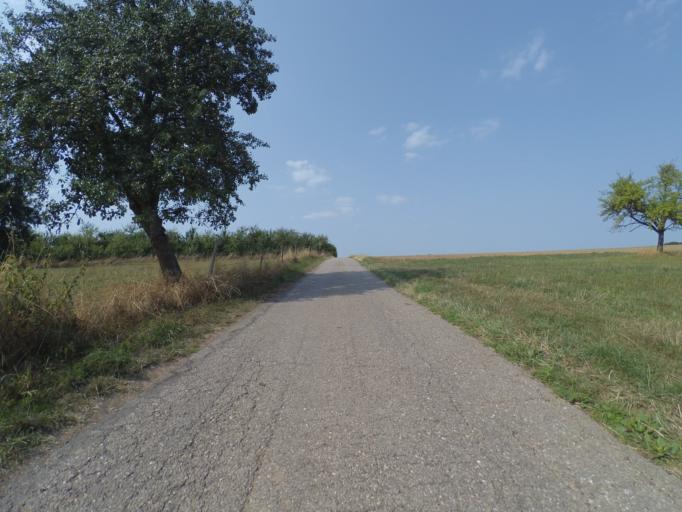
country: DE
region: Rheinland-Pfalz
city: Kirf
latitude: 49.5326
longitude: 6.5008
